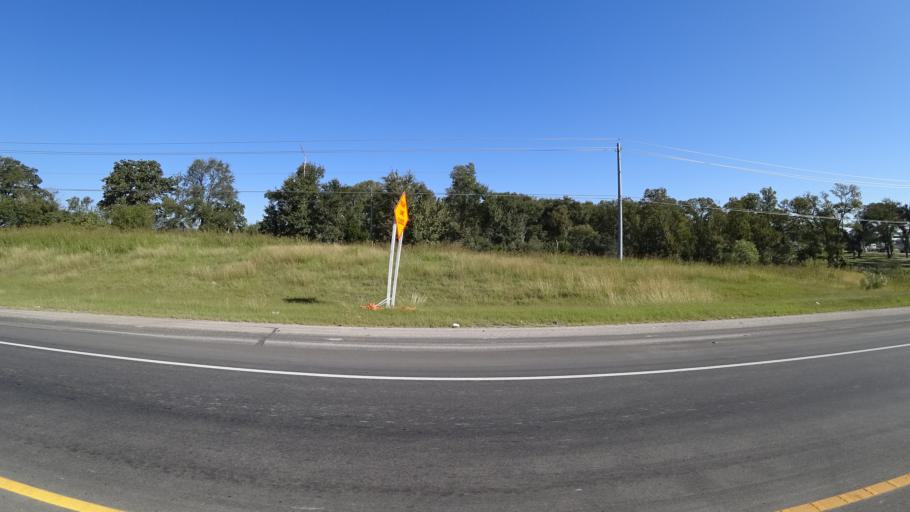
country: US
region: Texas
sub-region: Travis County
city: Hornsby Bend
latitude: 30.2549
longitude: -97.6077
